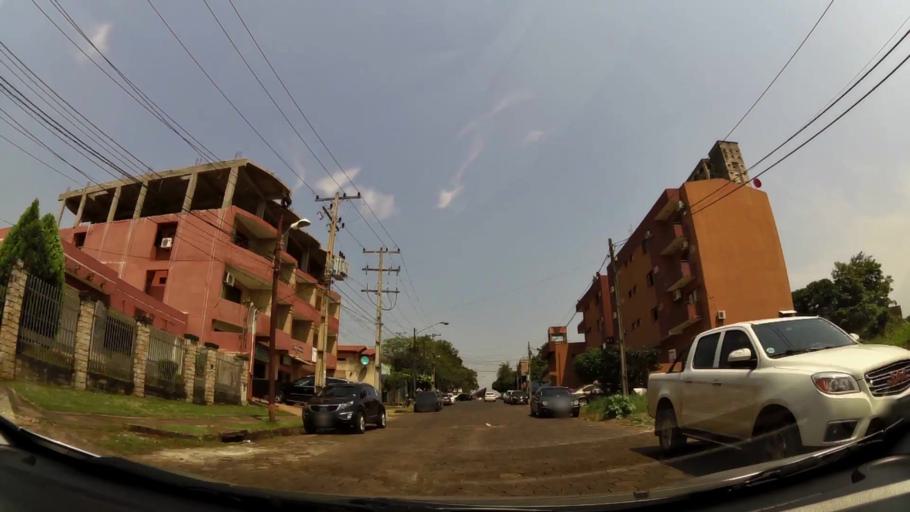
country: PY
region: Alto Parana
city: Presidente Franco
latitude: -25.5258
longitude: -54.6090
